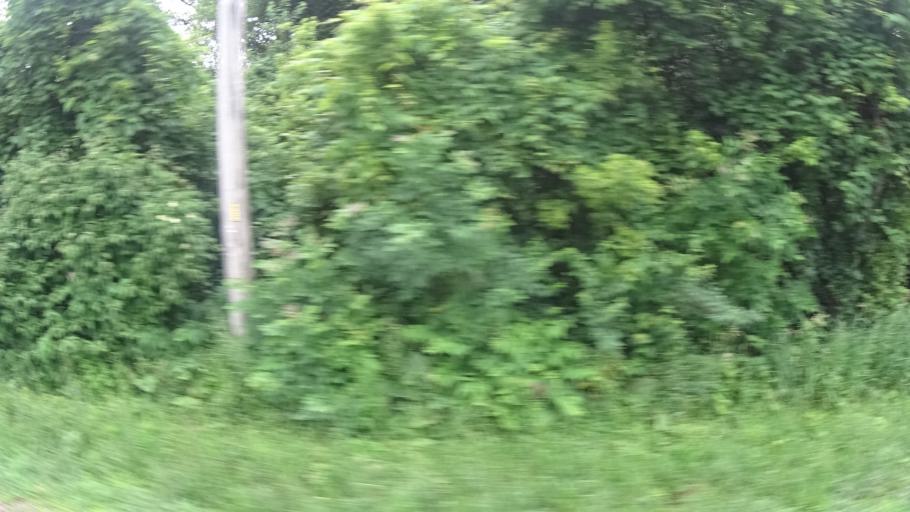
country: US
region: Ohio
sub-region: Erie County
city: Milan
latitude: 41.3330
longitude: -82.6083
